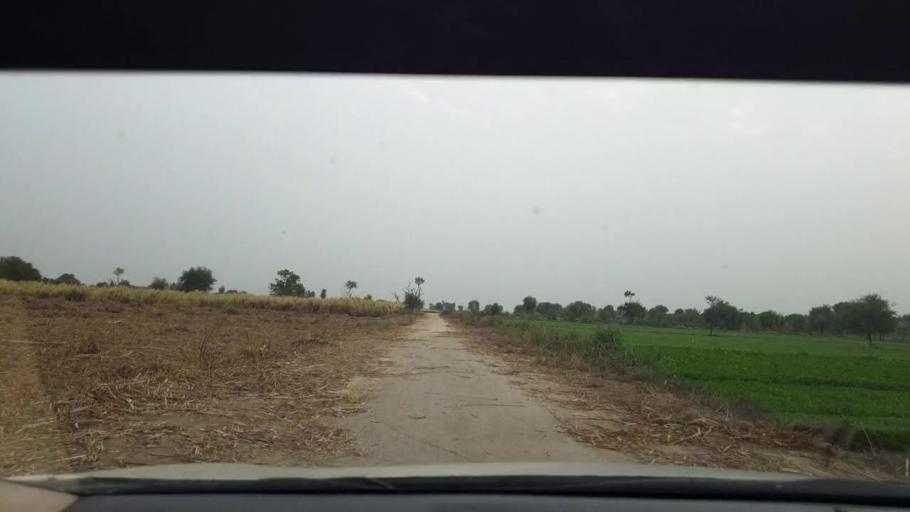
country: PK
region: Sindh
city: Jhol
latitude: 25.9264
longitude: 68.8534
